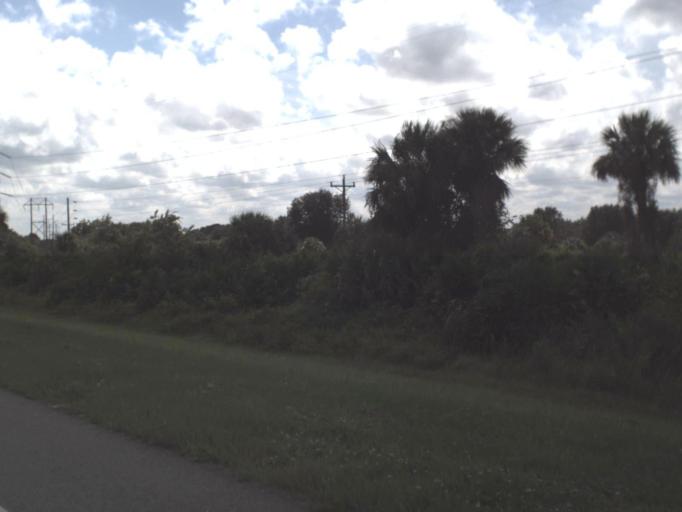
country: US
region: Florida
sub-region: Collier County
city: Immokalee
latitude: 26.3644
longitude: -81.3484
